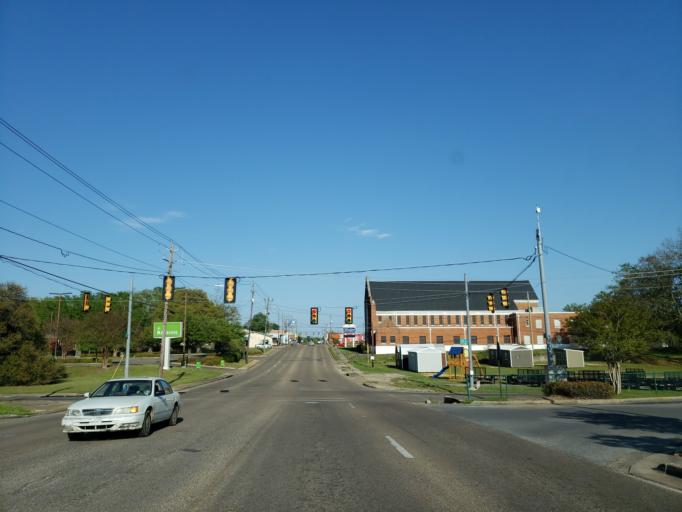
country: US
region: Mississippi
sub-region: Jones County
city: Laurel
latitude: 31.6945
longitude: -89.1458
